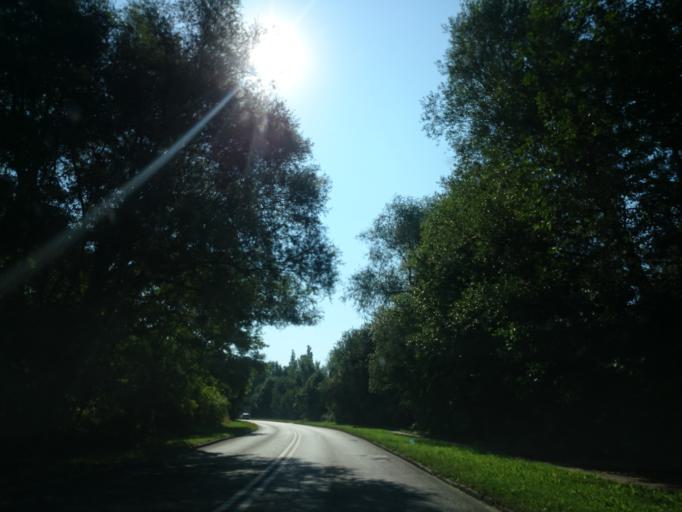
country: PL
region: West Pomeranian Voivodeship
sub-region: Szczecin
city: Szczecin
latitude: 53.3648
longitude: 14.6099
